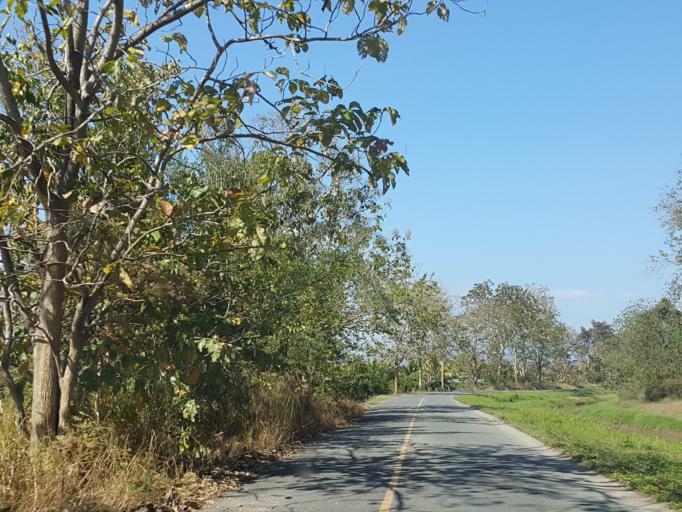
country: TH
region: Chiang Mai
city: Mae Taeng
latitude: 19.0793
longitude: 98.9542
